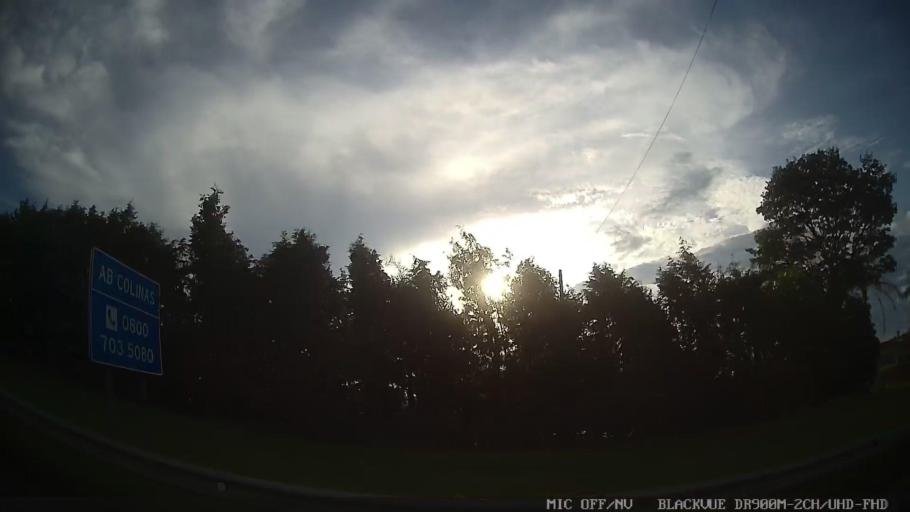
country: BR
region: Sao Paulo
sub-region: Tiete
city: Tiete
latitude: -23.1695
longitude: -47.6439
